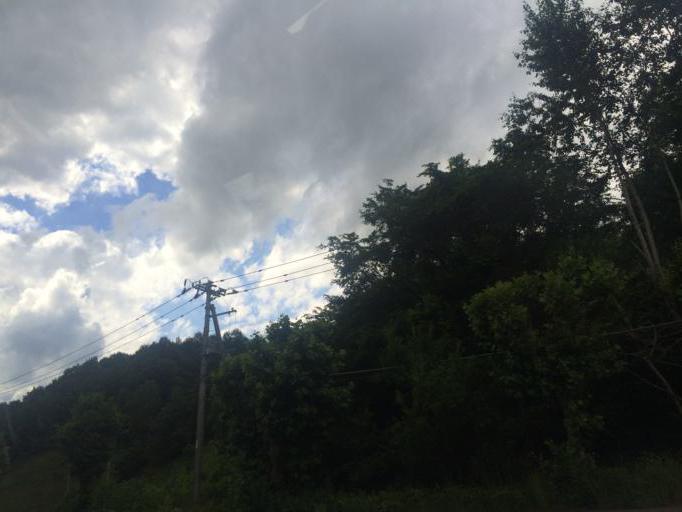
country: JP
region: Hokkaido
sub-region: Asahikawa-shi
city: Asahikawa
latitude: 43.7697
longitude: 142.3030
